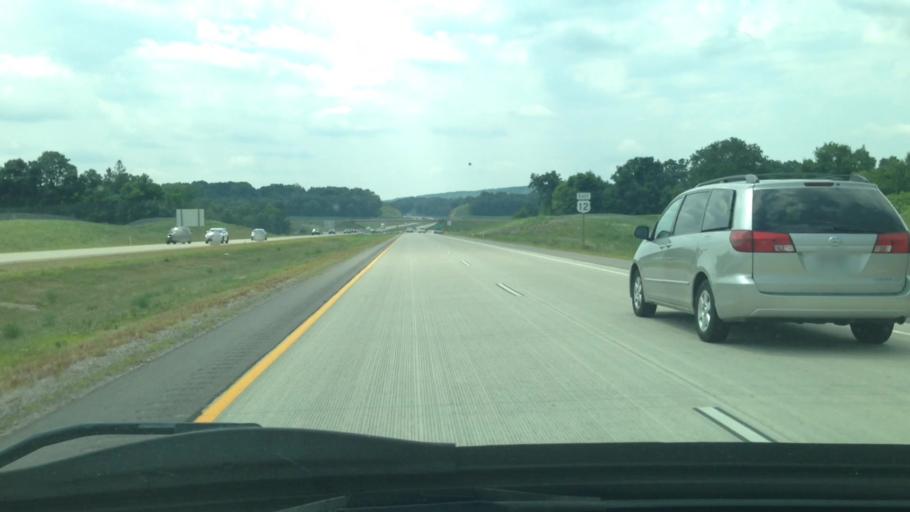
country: US
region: Wisconsin
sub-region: Sauk County
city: West Baraboo
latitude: 43.4524
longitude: -89.7782
